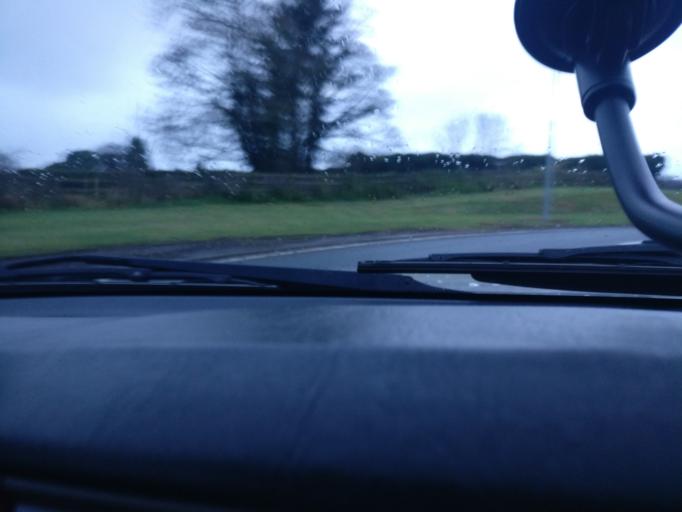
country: IE
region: Connaught
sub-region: County Galway
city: Ballinasloe
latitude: 53.3146
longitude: -8.2443
